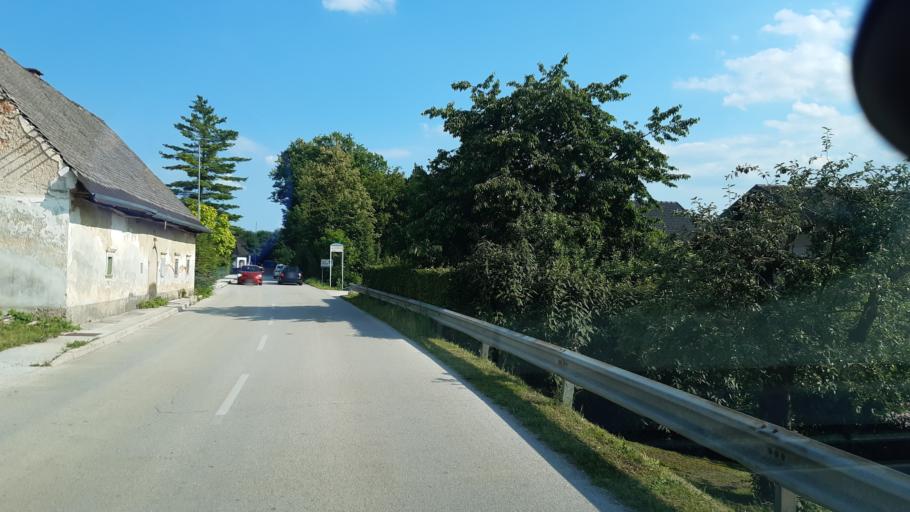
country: SI
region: Sencur
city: Hrastje
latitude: 46.2169
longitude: 14.3868
